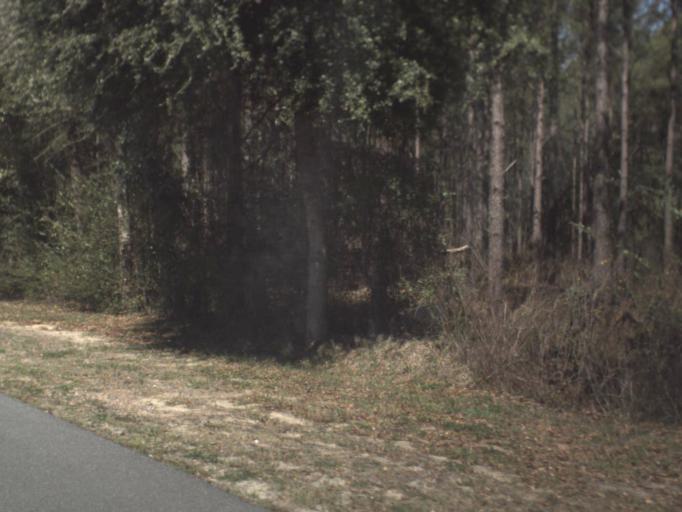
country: US
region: Florida
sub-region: Gadsden County
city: Gretna
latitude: 30.5996
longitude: -84.6507
